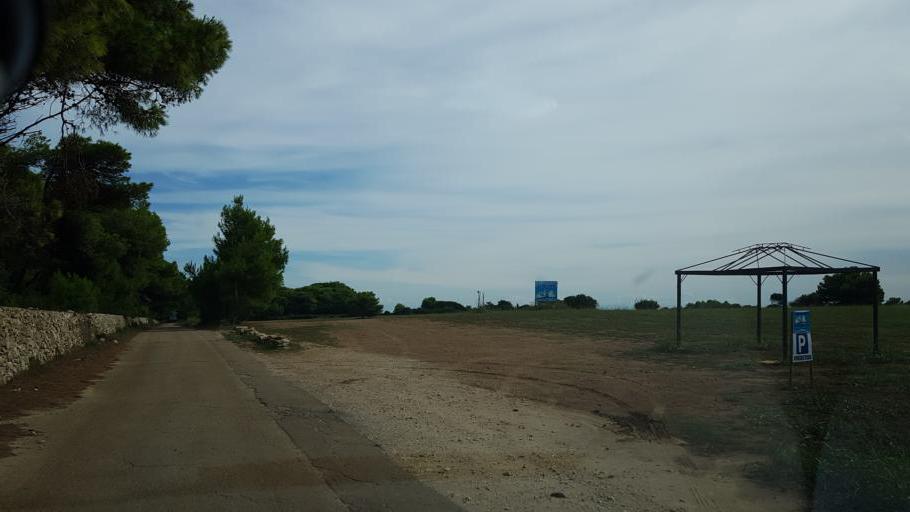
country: IT
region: Apulia
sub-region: Provincia di Lecce
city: Borgagne
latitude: 40.2663
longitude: 18.4350
